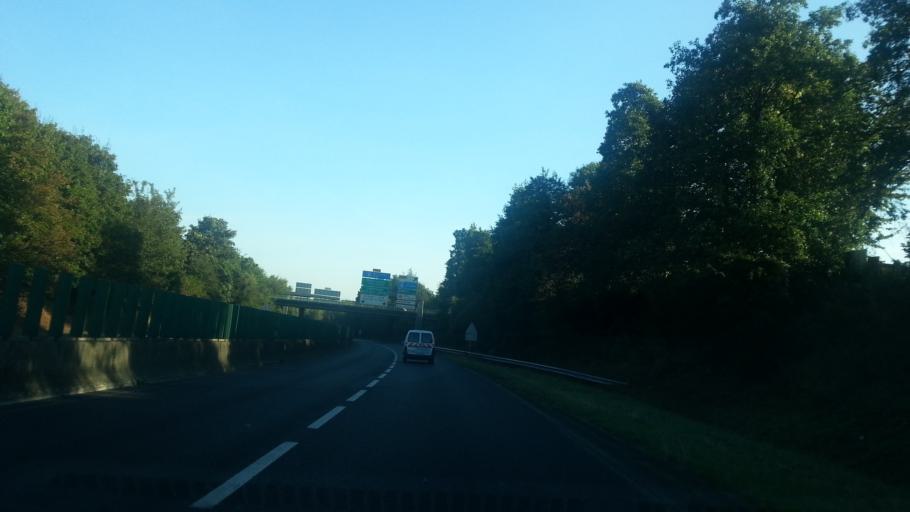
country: FR
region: Picardie
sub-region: Departement de l'Oise
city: Creil
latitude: 49.2536
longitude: 2.4914
